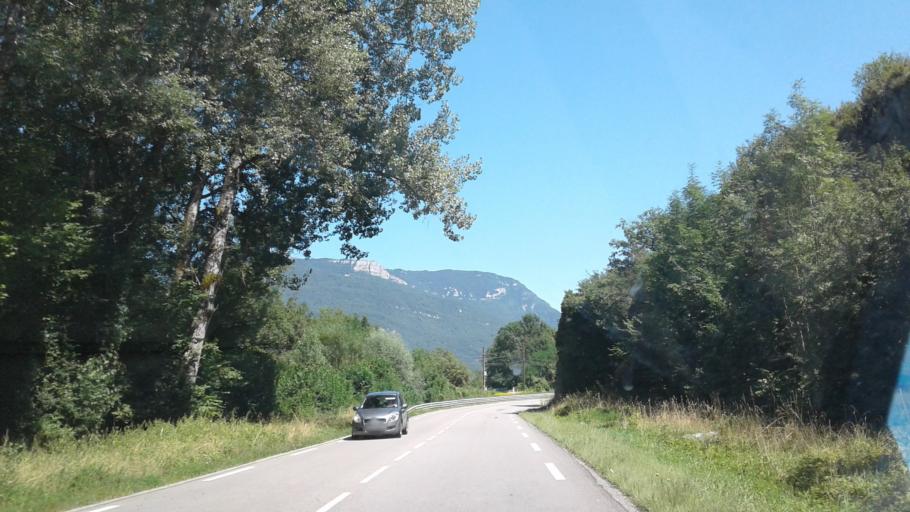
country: FR
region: Rhone-Alpes
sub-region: Departement de l'Ain
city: Artemare
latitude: 45.8632
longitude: 5.6735
